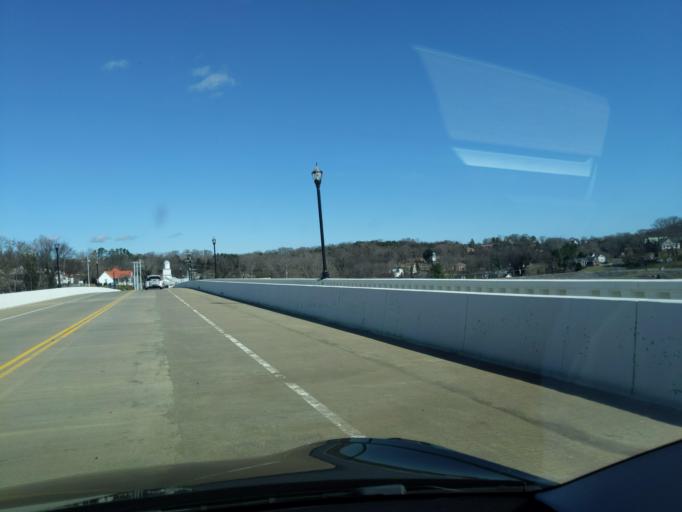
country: US
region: Tennessee
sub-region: Jefferson County
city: Dandridge
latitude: 36.0126
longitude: -83.4134
